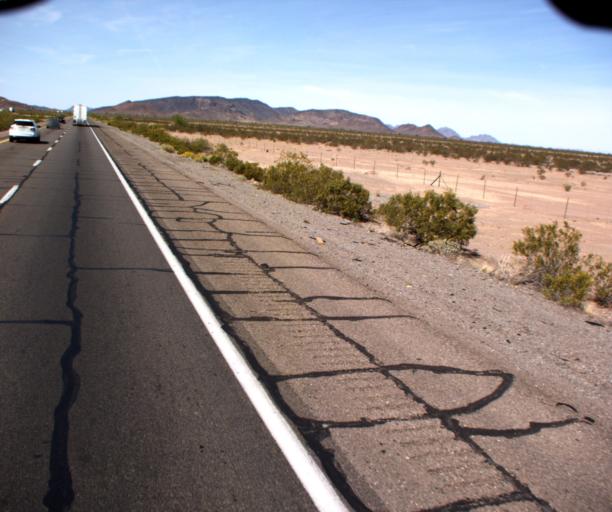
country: US
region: Arizona
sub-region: La Paz County
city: Salome
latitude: 33.6413
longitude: -113.8388
